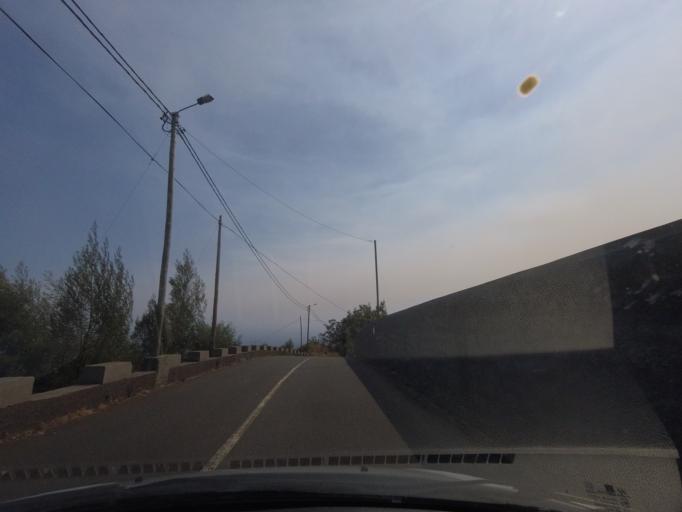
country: PT
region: Madeira
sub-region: Ribeira Brava
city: Campanario
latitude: 32.6908
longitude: -17.0571
